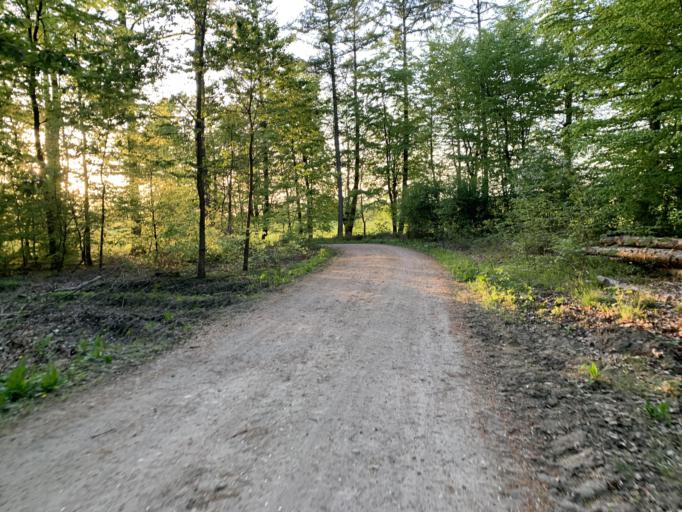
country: DE
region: Schleswig-Holstein
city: Worth
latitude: 53.4669
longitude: 10.4245
